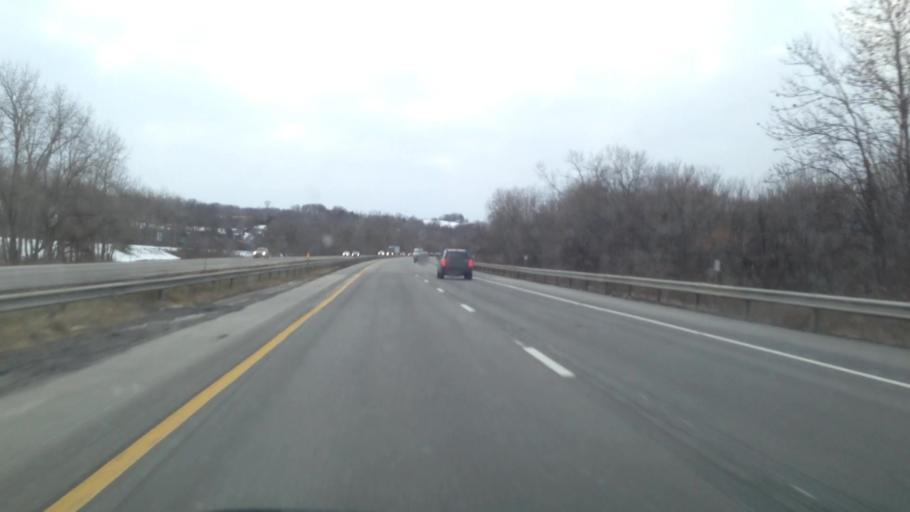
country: US
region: New York
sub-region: Montgomery County
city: Canajoharie
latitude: 42.8934
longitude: -74.5199
